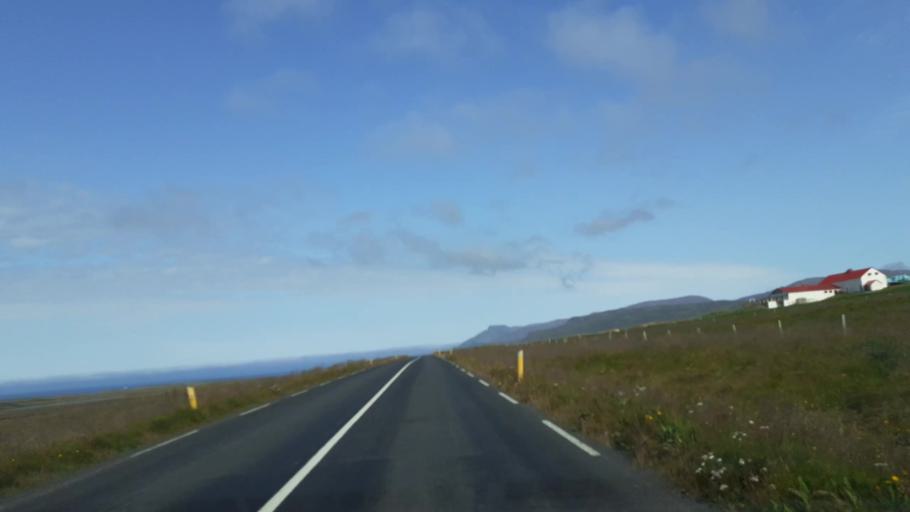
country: IS
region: Northwest
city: Saudarkrokur
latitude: 65.6902
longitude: -20.2367
